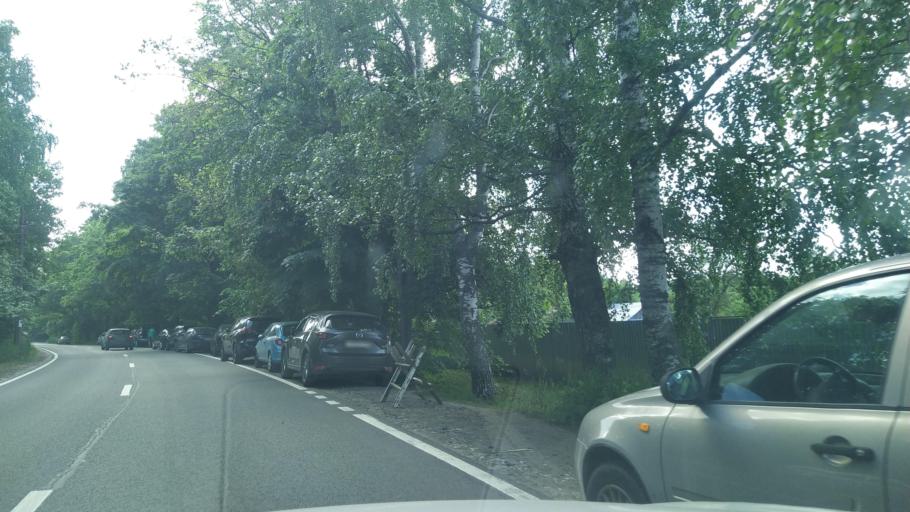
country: RU
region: St.-Petersburg
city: Kronshtadt
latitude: 60.0246
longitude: 29.6836
